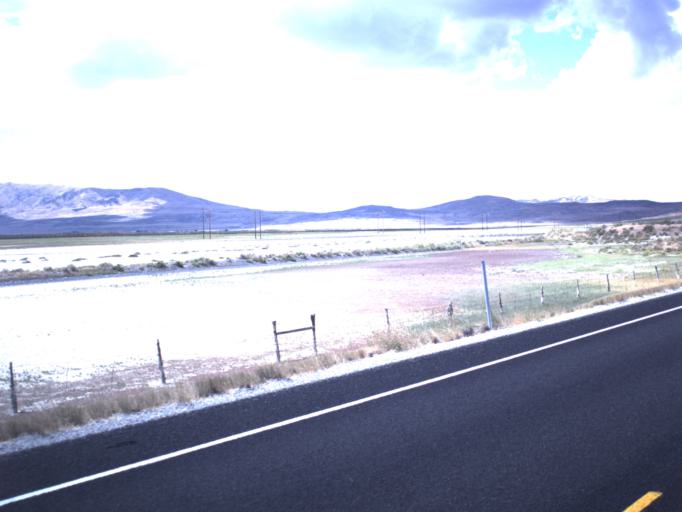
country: US
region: Utah
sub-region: Box Elder County
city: Tremonton
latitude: 41.6239
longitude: -112.3919
